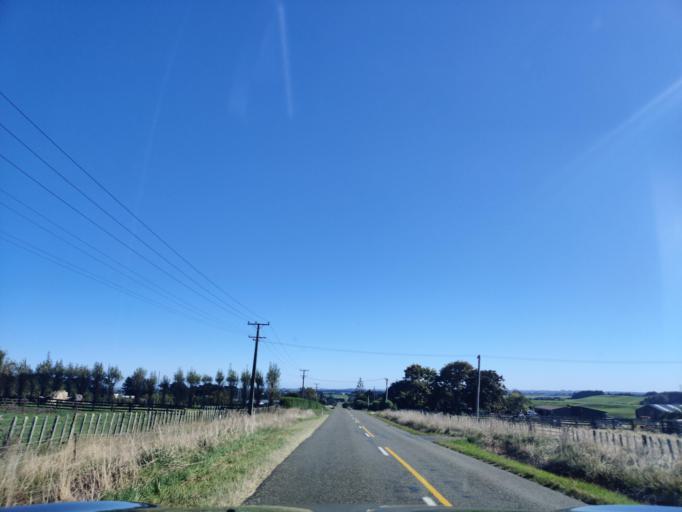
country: NZ
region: Manawatu-Wanganui
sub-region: Palmerston North City
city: Palmerston North
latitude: -40.2442
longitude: 175.6745
